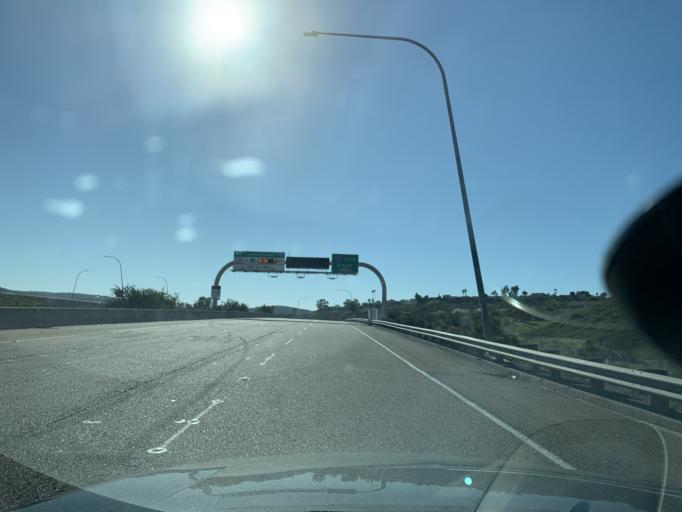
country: US
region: California
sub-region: San Diego County
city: Poway
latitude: 32.9609
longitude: -117.0987
